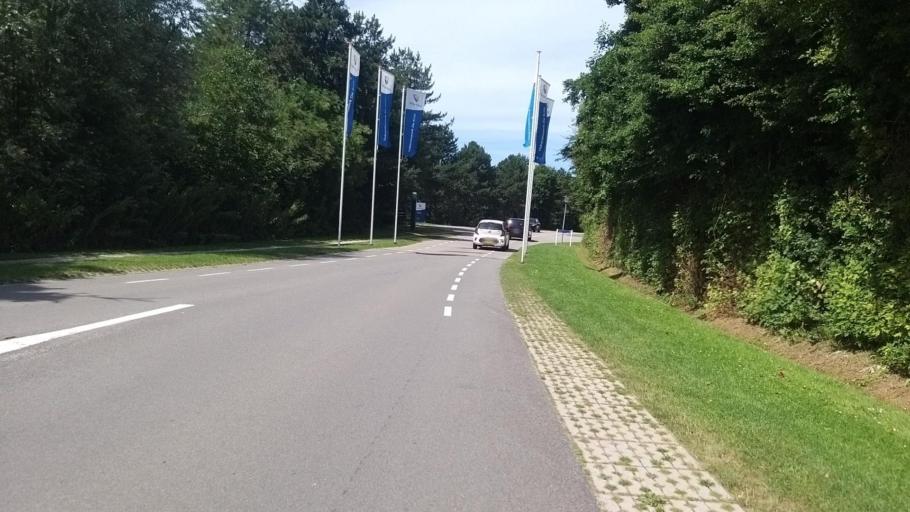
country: NL
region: North Holland
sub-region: Gemeente Texel
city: Den Burg
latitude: 53.1490
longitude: 4.8626
